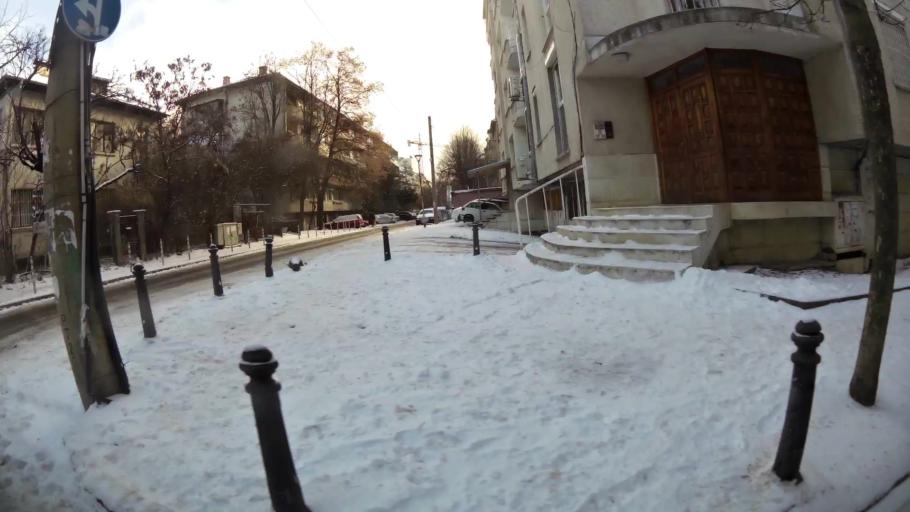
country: BG
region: Sofia-Capital
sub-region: Stolichna Obshtina
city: Sofia
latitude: 42.6702
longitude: 23.3263
